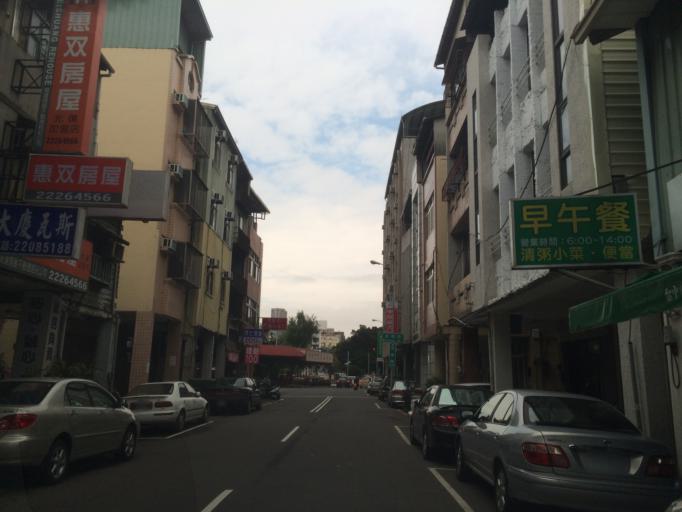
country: TW
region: Taiwan
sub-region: Taichung City
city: Taichung
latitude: 24.1448
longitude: 120.6799
